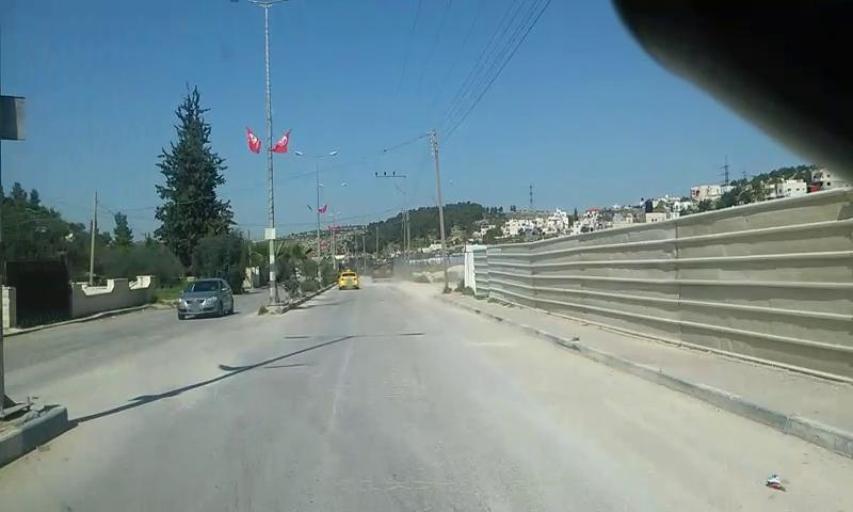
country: PS
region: West Bank
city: Idhna
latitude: 31.5703
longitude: 34.9811
